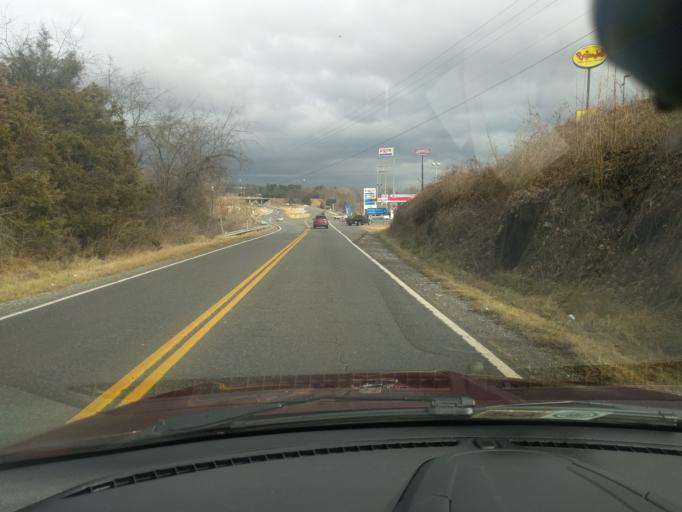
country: US
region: Virginia
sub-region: Pulaski County
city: Dublin
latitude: 37.0743
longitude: -80.6951
